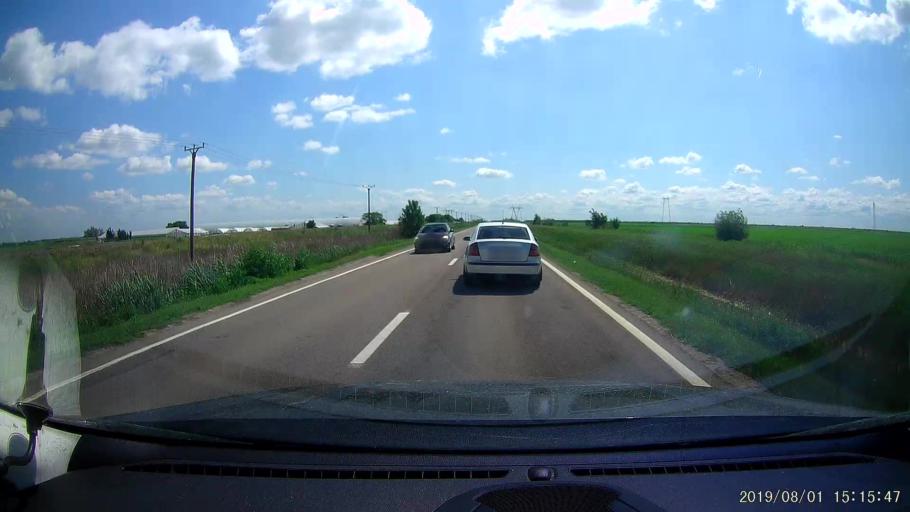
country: RO
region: Braila
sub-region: Comuna Tichilesti
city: Tichilesti
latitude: 45.1588
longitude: 27.8632
